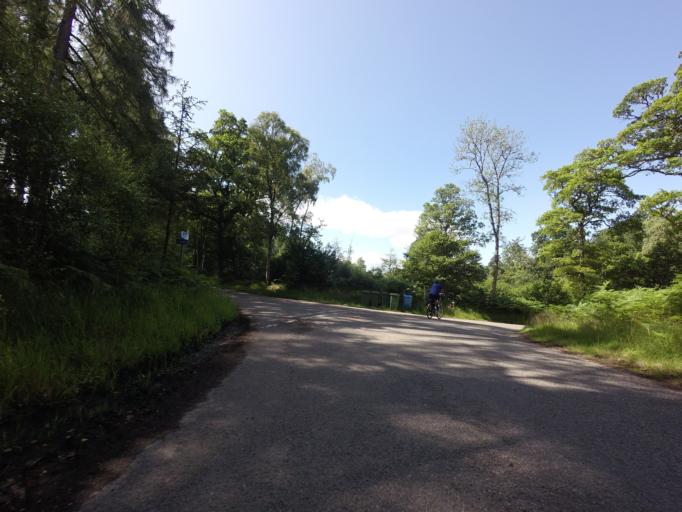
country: GB
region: Scotland
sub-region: Highland
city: Nairn
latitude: 57.5041
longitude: -3.9099
